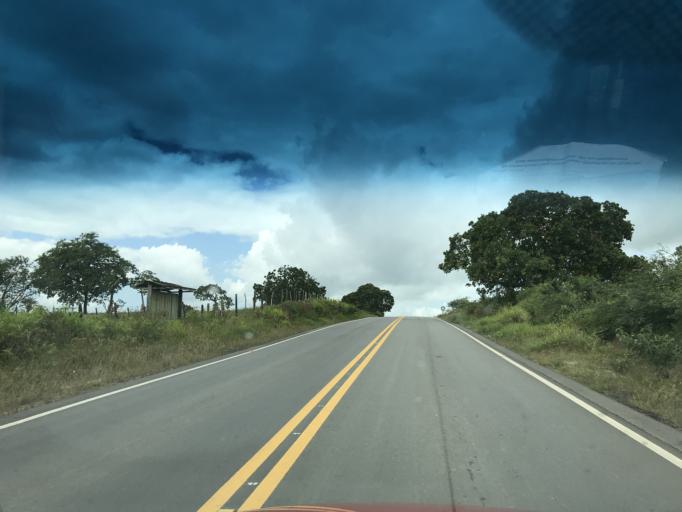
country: BR
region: Bahia
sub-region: Conceicao Do Almeida
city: Conceicao do Almeida
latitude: -12.6838
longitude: -39.2534
